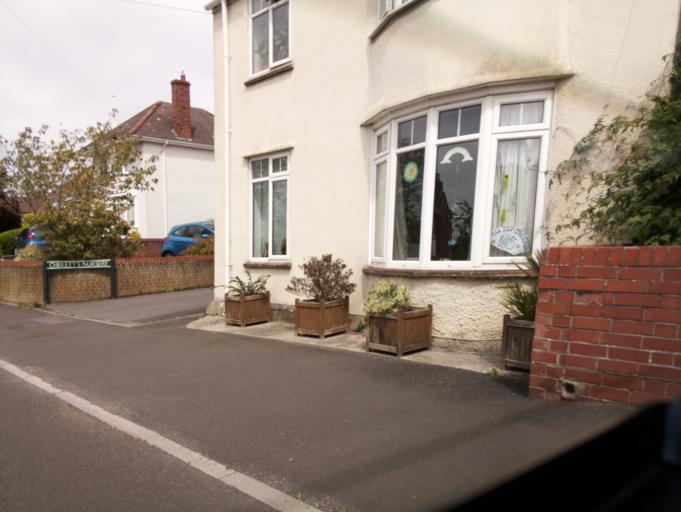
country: GB
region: England
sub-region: Somerset
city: Glastonbury
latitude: 51.1531
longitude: -2.7144
